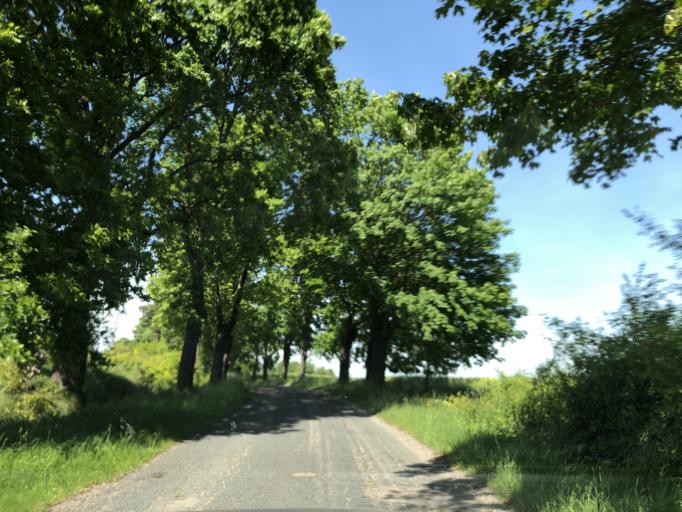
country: PL
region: West Pomeranian Voivodeship
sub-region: Powiat kolobrzeski
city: Goscino
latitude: 54.0301
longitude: 15.7352
